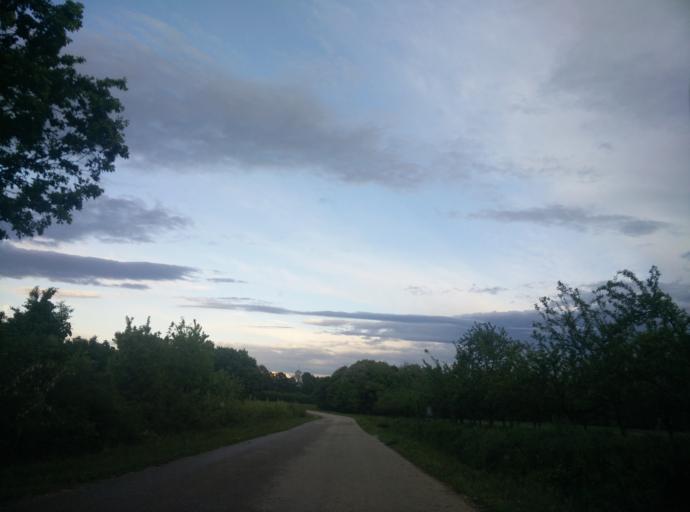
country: BA
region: Brcko
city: Brcko
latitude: 44.7839
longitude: 18.8169
